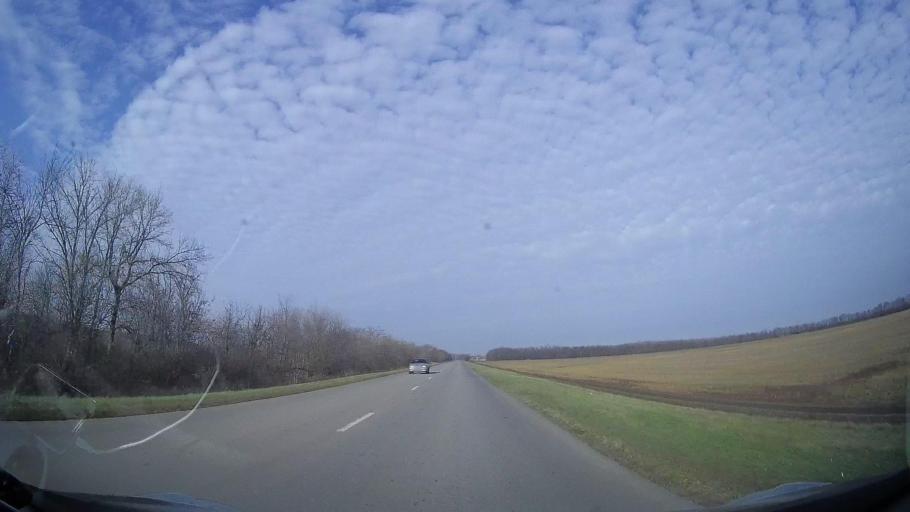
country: RU
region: Rostov
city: Gigant
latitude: 46.8278
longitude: 41.3377
